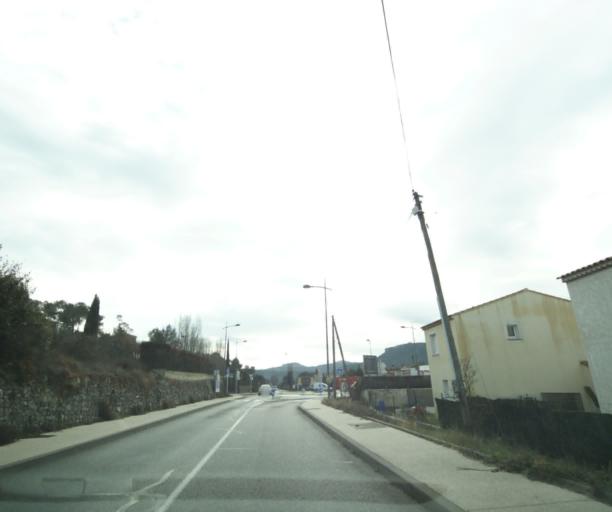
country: FR
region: Provence-Alpes-Cote d'Azur
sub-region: Departement du Var
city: Tourves
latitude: 43.4150
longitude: 5.9175
